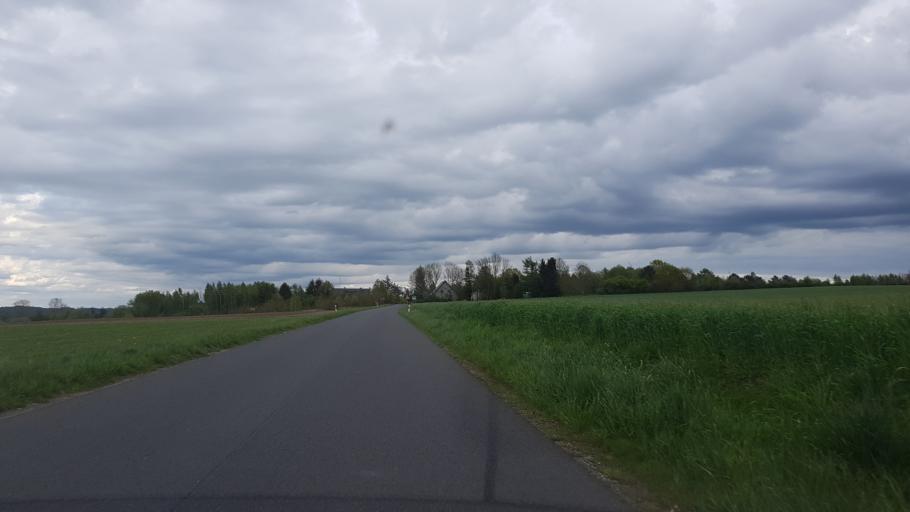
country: PL
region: West Pomeranian Voivodeship
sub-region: Powiat slawienski
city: Darlowo
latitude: 54.2731
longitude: 16.5165
